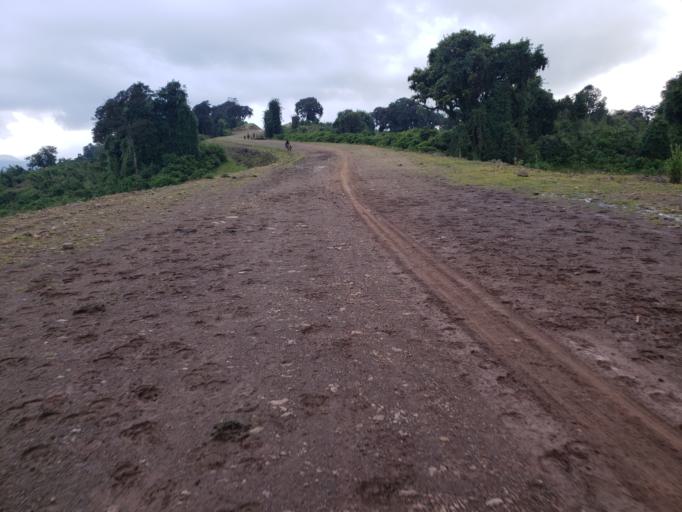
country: ET
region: Oromiya
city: Dodola
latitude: 6.6621
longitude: 39.3643
